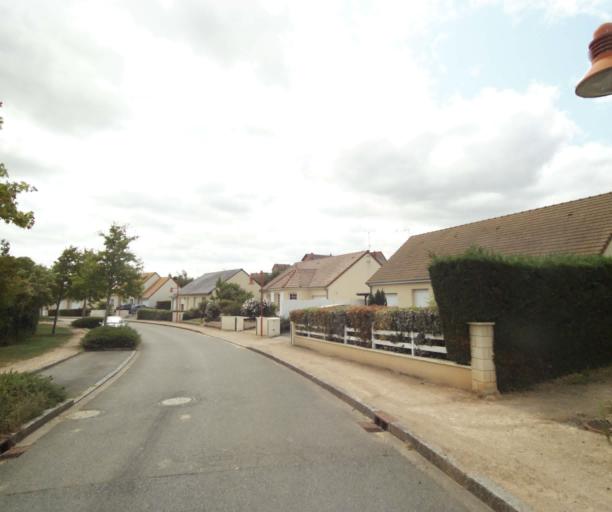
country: FR
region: Pays de la Loire
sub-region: Departement de la Sarthe
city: Sable-sur-Sarthe
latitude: 47.8495
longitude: -0.3486
